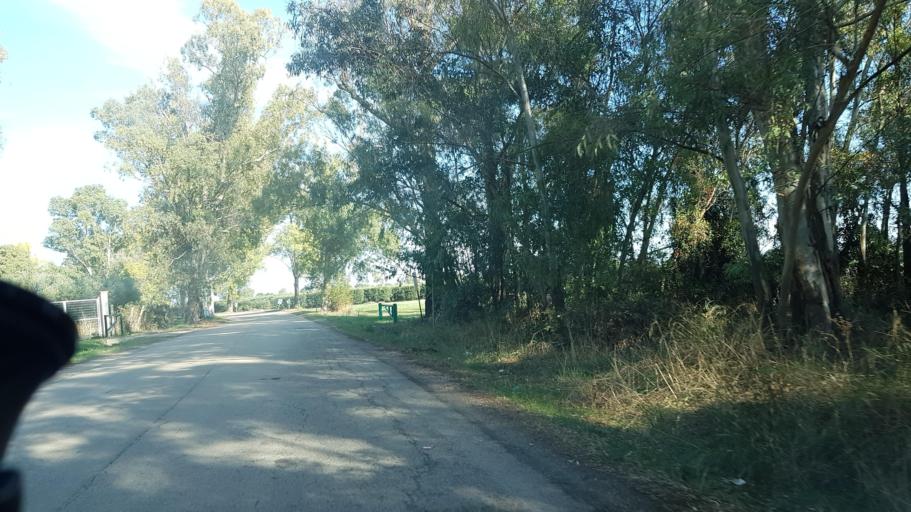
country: IT
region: Apulia
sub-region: Provincia di Foggia
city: Carapelle
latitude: 41.3890
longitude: 15.6492
